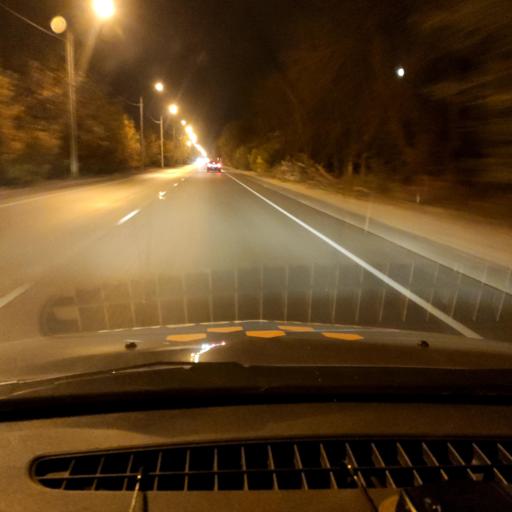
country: RU
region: Voronezj
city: Shilovo
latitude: 51.5786
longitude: 39.1534
